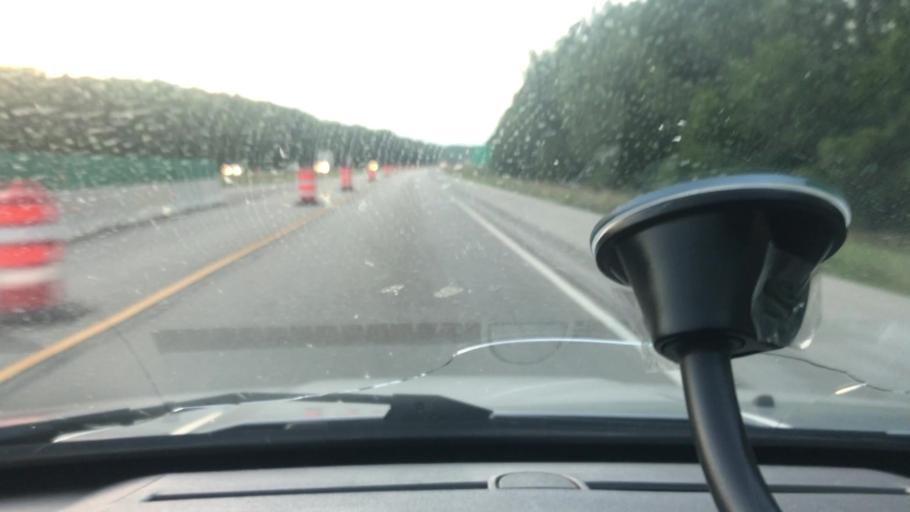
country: US
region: Illinois
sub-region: Peoria County
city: Bartonville
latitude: 40.6405
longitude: -89.6284
